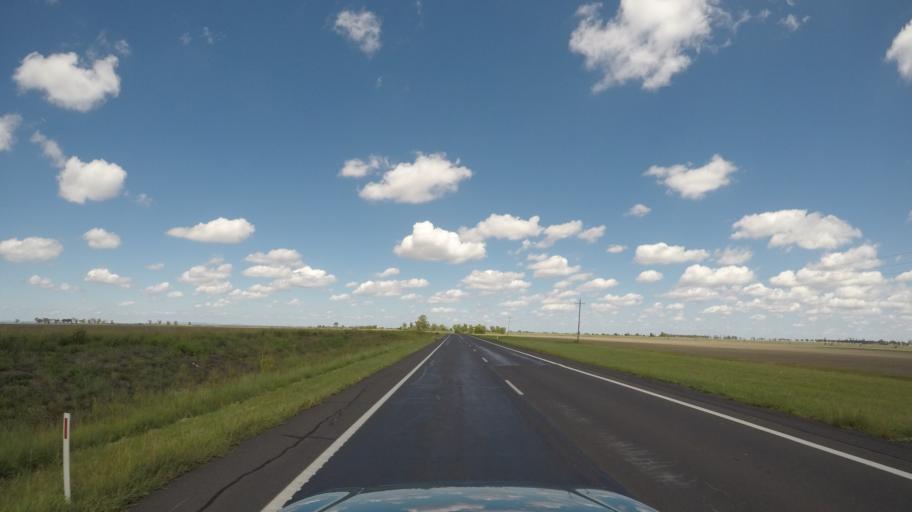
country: AU
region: Queensland
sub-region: Toowoomba
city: Westbrook
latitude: -27.7527
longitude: 151.5195
